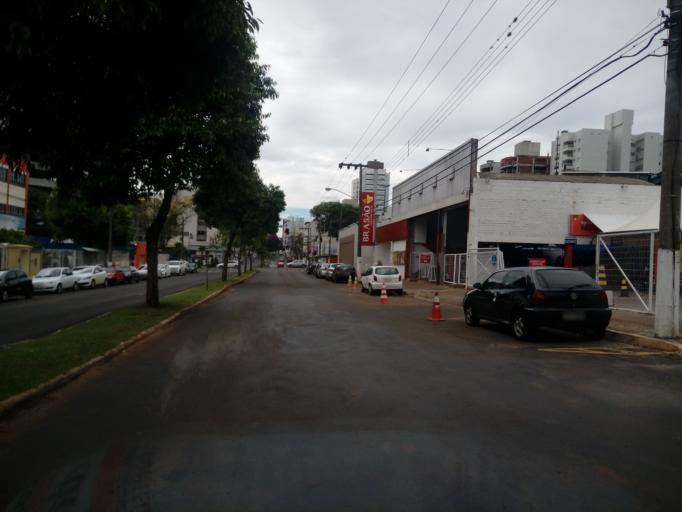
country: BR
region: Santa Catarina
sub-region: Chapeco
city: Chapeco
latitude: -27.1072
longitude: -52.6168
